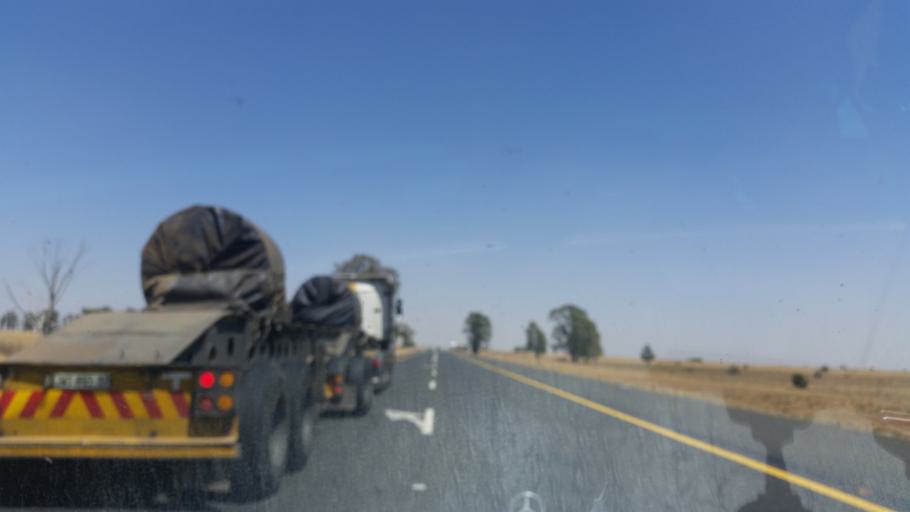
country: ZA
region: Orange Free State
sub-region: Lejweleputswa District Municipality
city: Winburg
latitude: -28.6395
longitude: 26.8919
